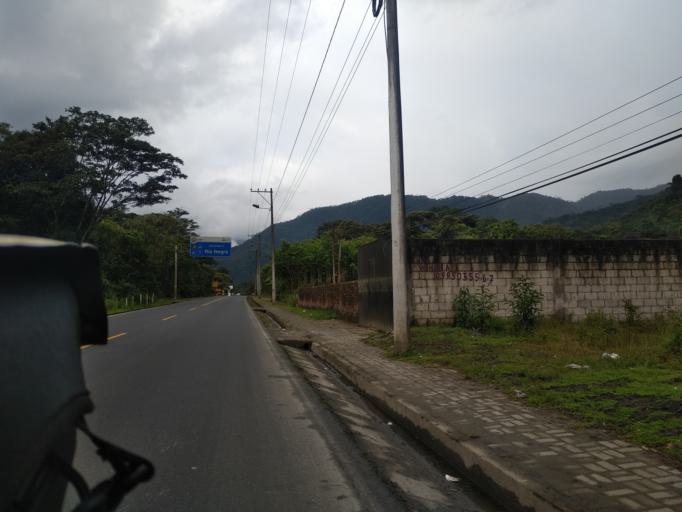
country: EC
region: Tungurahua
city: Banos
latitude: -1.4138
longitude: -78.2191
